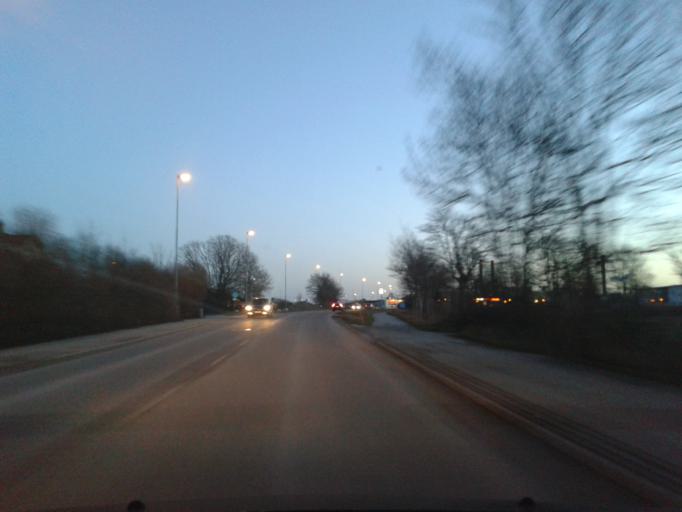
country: SE
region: Gotland
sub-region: Gotland
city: Visby
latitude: 57.6288
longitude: 18.3165
